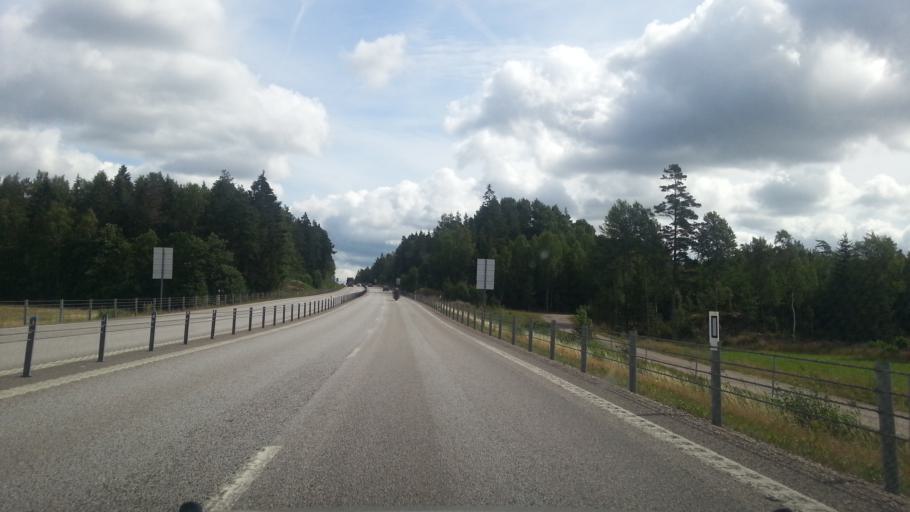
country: SE
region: Vaestra Goetaland
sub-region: Gullspangs Kommun
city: Hova
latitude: 58.8059
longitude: 14.1047
